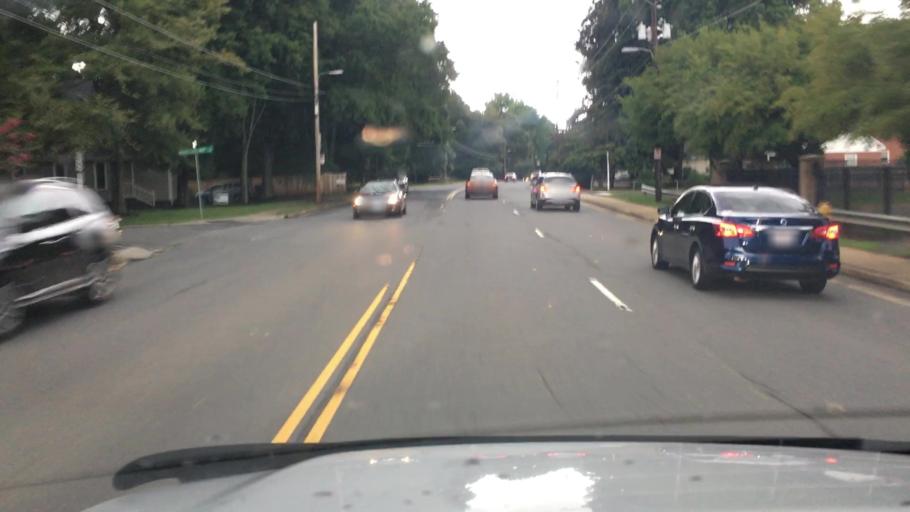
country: US
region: North Carolina
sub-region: Mecklenburg County
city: Matthews
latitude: 35.1451
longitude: -80.8015
